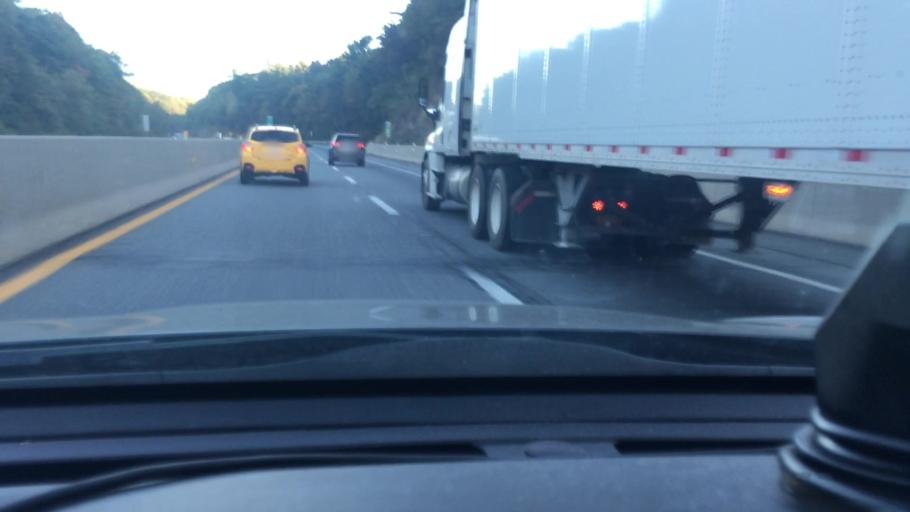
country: US
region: Pennsylvania
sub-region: Carbon County
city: Weissport East
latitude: 40.9117
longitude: -75.6459
